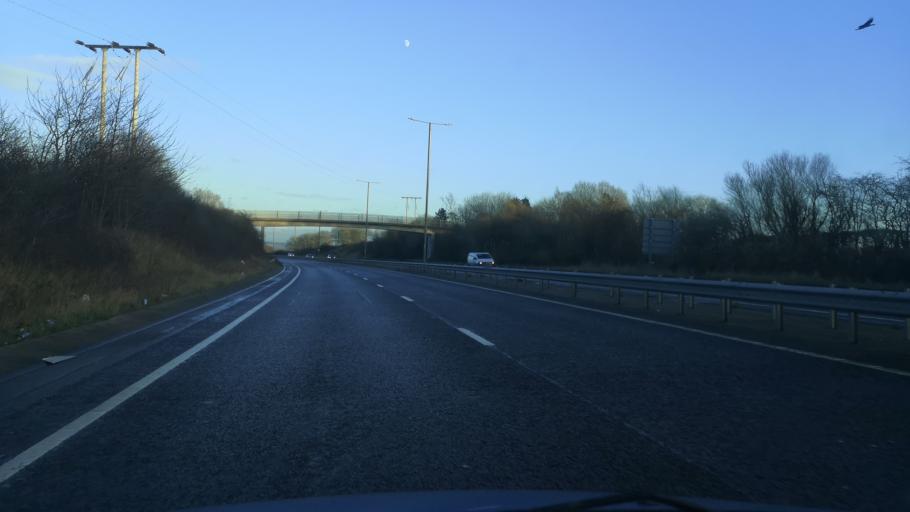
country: GB
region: England
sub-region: Barnsley
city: Hoyland Nether
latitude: 53.5102
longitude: -1.4262
